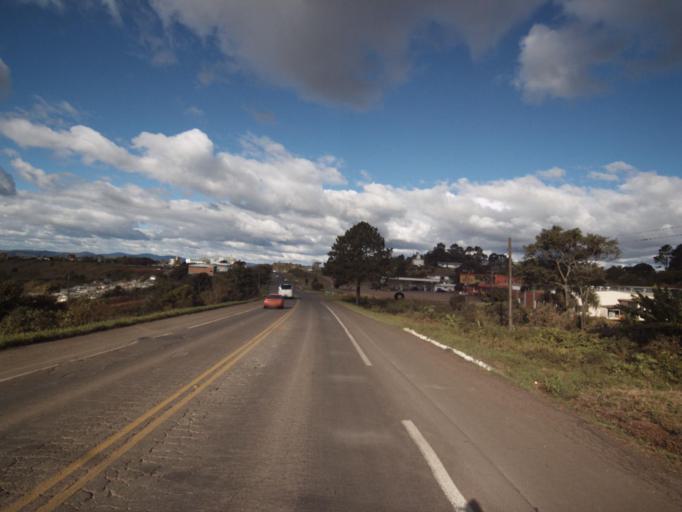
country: BR
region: Santa Catarina
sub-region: Joacaba
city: Joacaba
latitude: -27.1767
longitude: -51.5479
